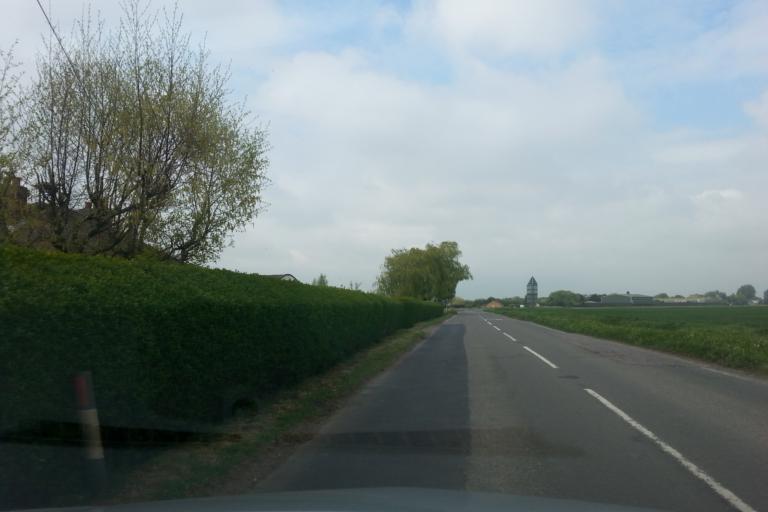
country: GB
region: England
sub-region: Norfolk
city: Outwell
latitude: 52.5904
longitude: 0.2276
